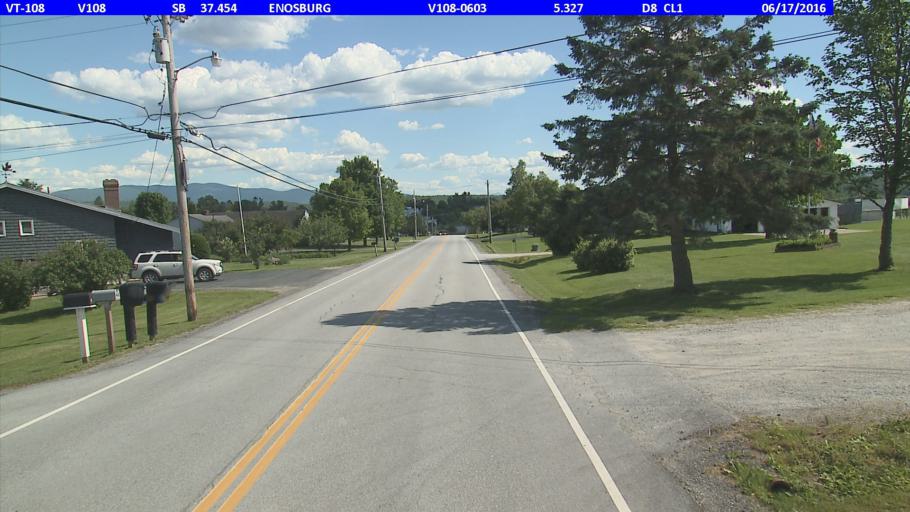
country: US
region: Vermont
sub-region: Franklin County
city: Enosburg Falls
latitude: 44.9171
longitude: -72.8058
